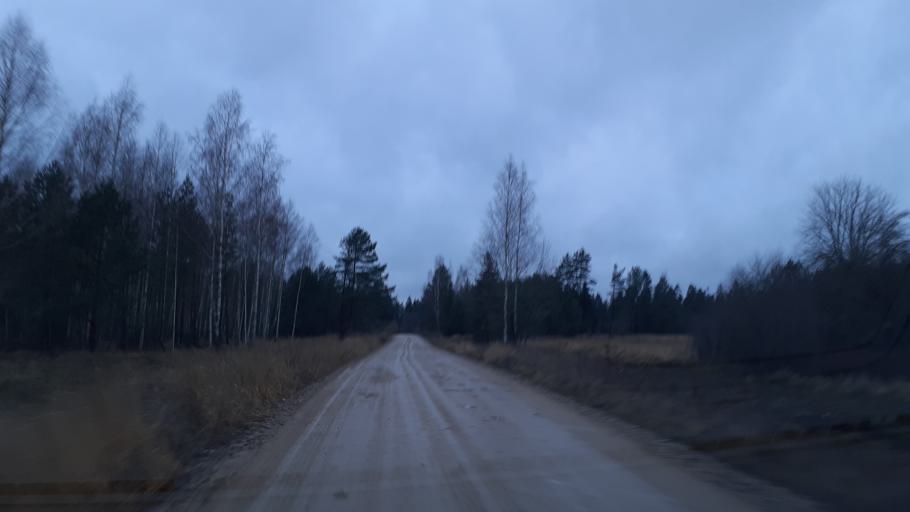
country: LV
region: Kuldigas Rajons
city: Kuldiga
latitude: 57.0535
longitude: 22.1200
